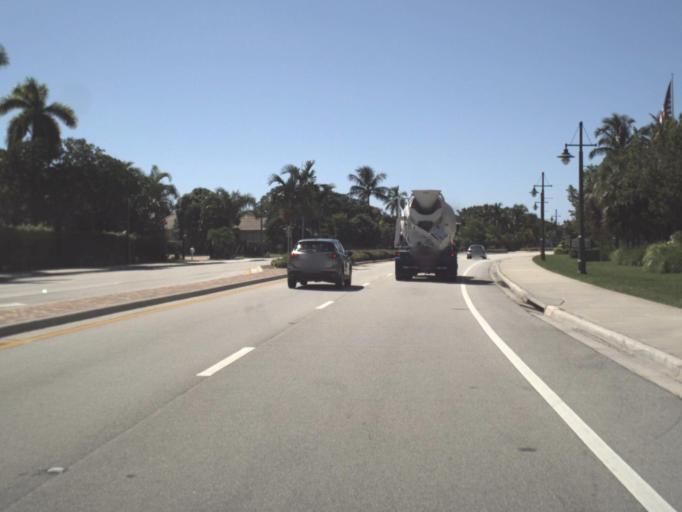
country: US
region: Florida
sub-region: Collier County
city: Marco
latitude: 25.9603
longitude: -81.7113
